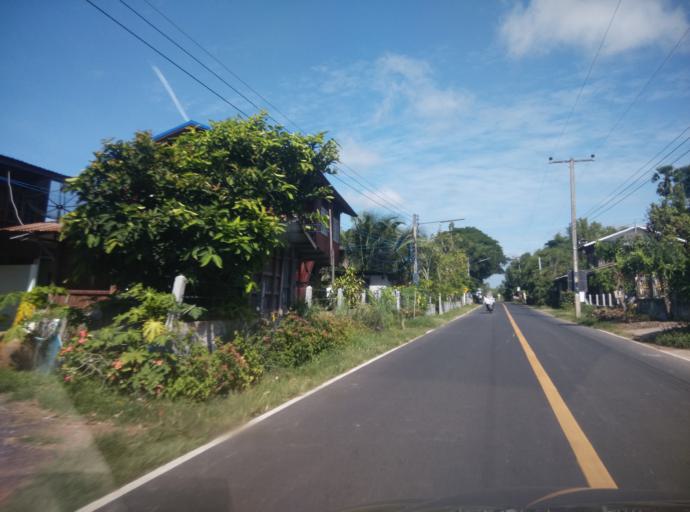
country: TH
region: Sisaket
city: Uthumphon Phisai
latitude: 15.1243
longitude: 104.1996
